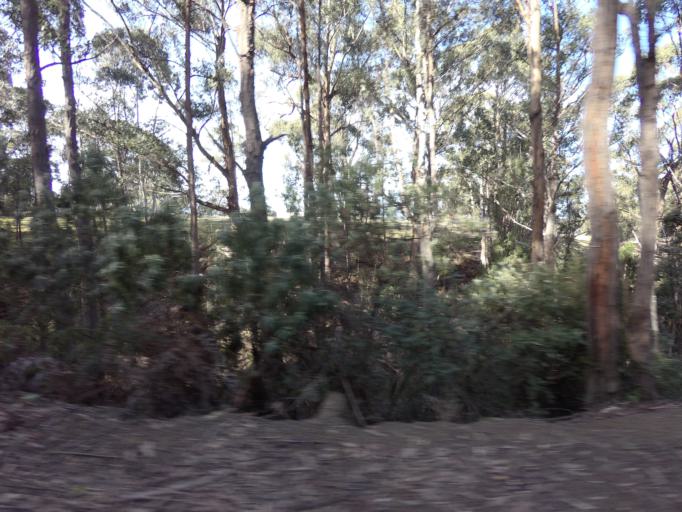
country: AU
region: Tasmania
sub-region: Kingborough
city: Kettering
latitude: -43.1012
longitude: 147.2611
